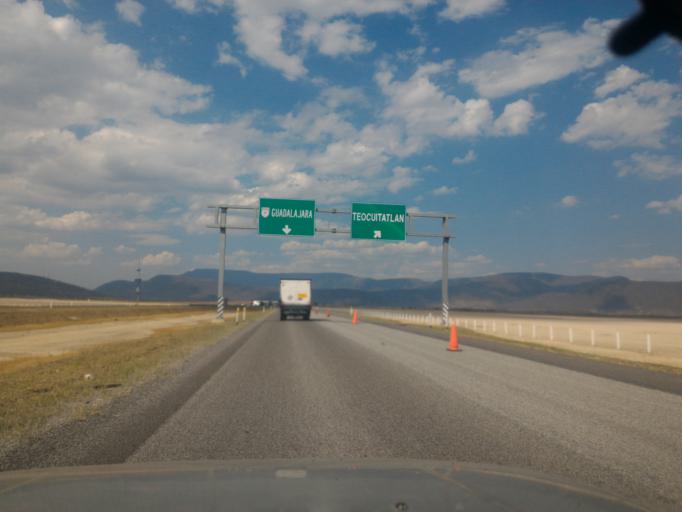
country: MX
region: Jalisco
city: Atoyac
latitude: 20.1193
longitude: -103.5096
